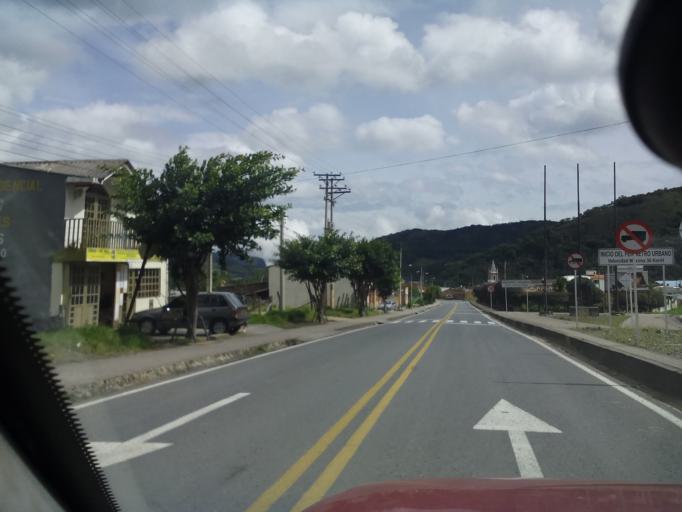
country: CO
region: Boyaca
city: Arcabuco
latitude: 5.7511
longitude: -73.4343
